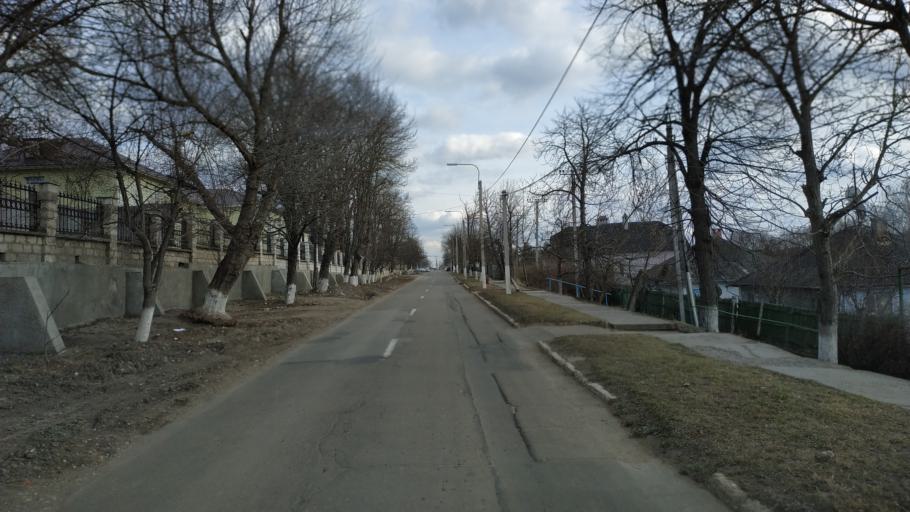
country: MD
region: Hincesti
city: Hincesti
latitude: 46.8341
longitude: 28.5794
